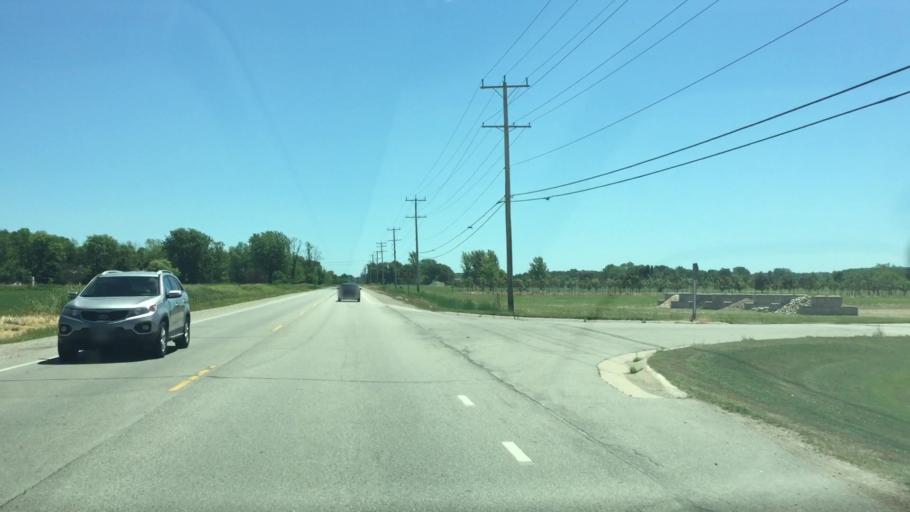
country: US
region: Wisconsin
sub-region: Calumet County
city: Sherwood
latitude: 44.1981
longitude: -88.3138
